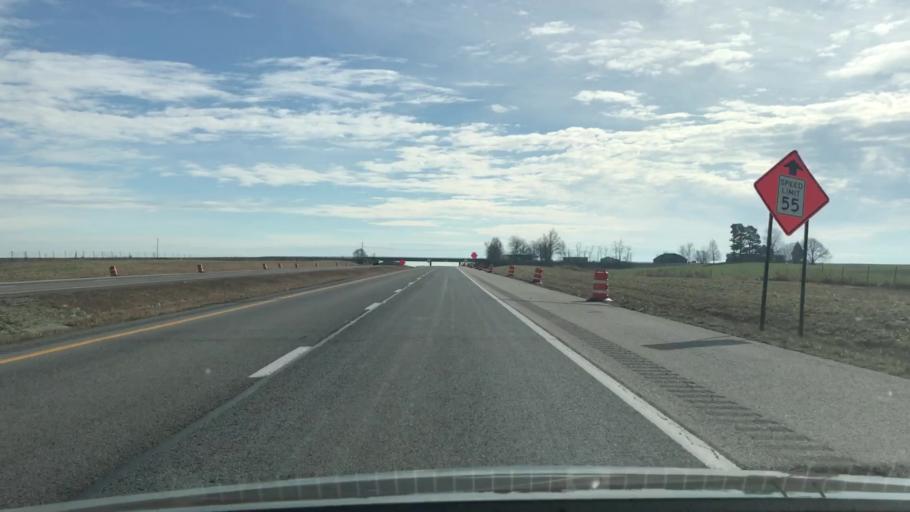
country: US
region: Kentucky
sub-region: Daviess County
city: Masonville
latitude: 37.6649
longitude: -87.0189
